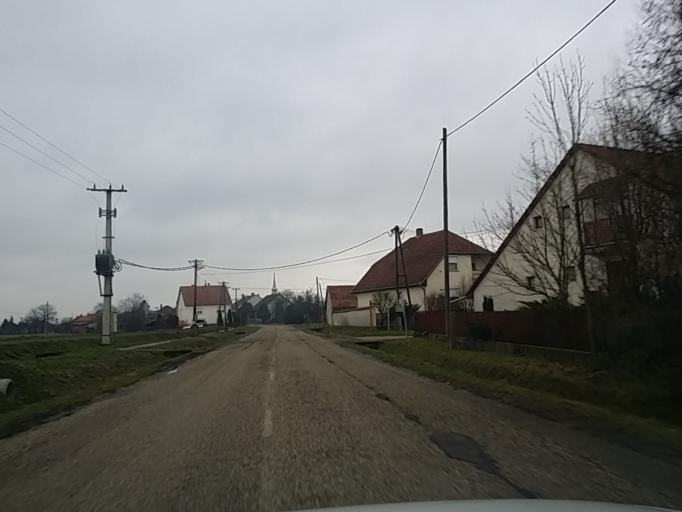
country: HU
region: Borsod-Abauj-Zemplen
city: Saly
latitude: 47.8907
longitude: 20.6745
